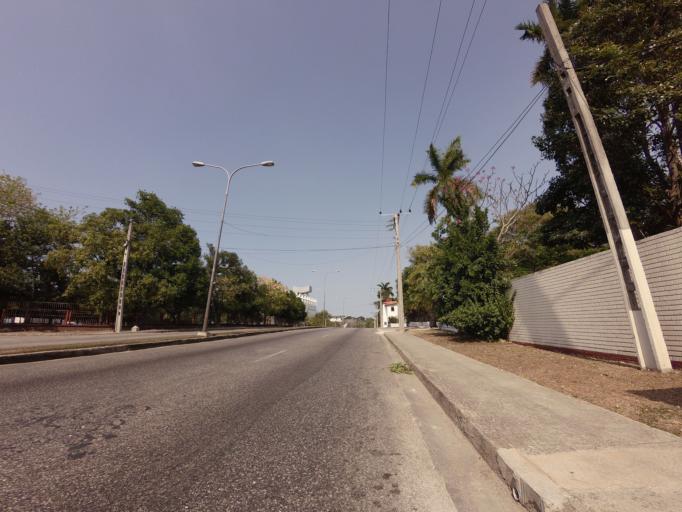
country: CU
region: La Habana
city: Cerro
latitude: 23.0767
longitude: -82.4541
